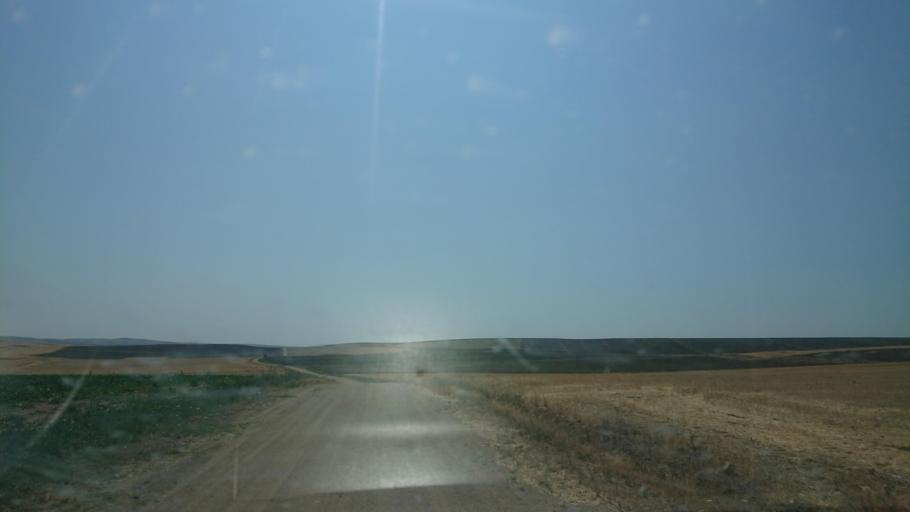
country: TR
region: Aksaray
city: Sariyahsi
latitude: 38.9565
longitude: 33.9150
